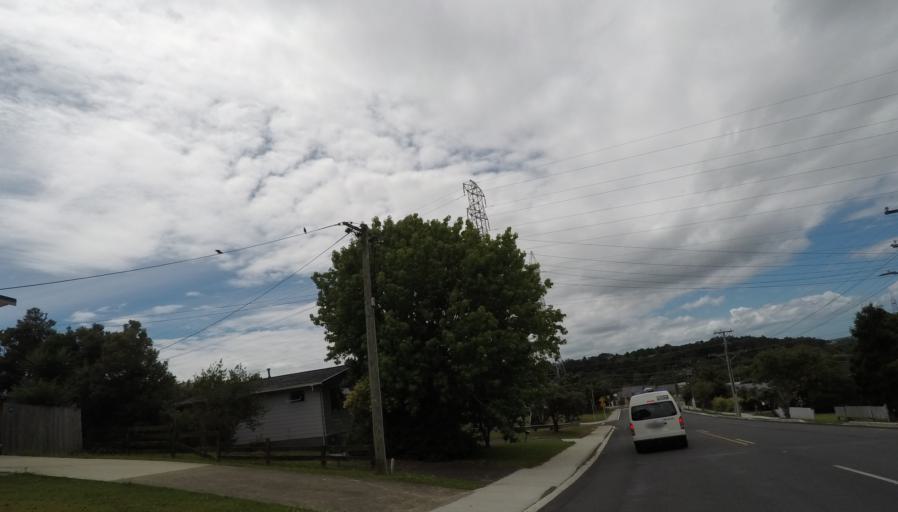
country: NZ
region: Auckland
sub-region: Auckland
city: Rosebank
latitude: -36.8456
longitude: 174.6243
